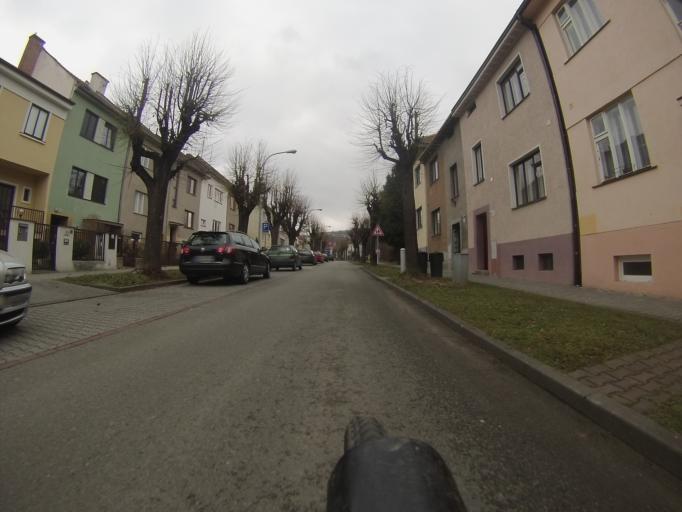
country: CZ
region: South Moravian
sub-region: Mesto Brno
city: Brno
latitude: 49.1975
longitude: 16.6506
